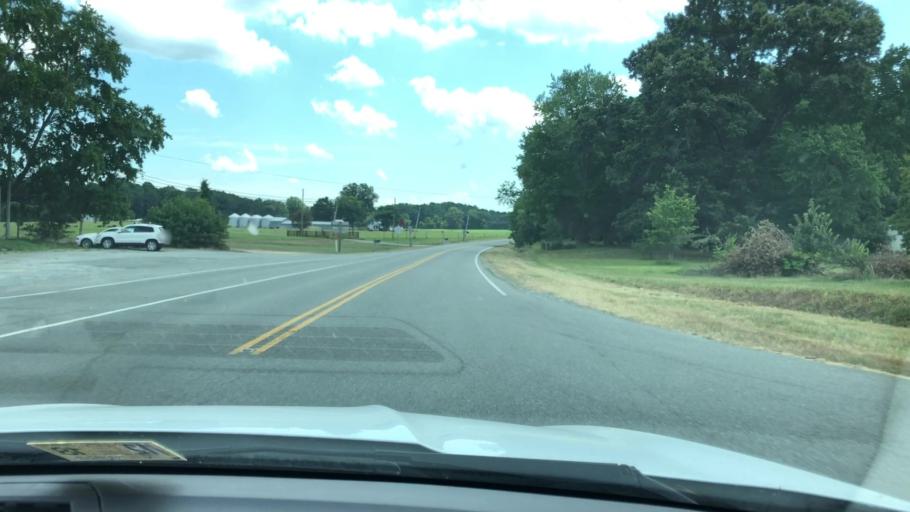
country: US
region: Virginia
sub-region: Lancaster County
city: Lancaster
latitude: 37.7957
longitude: -76.5216
